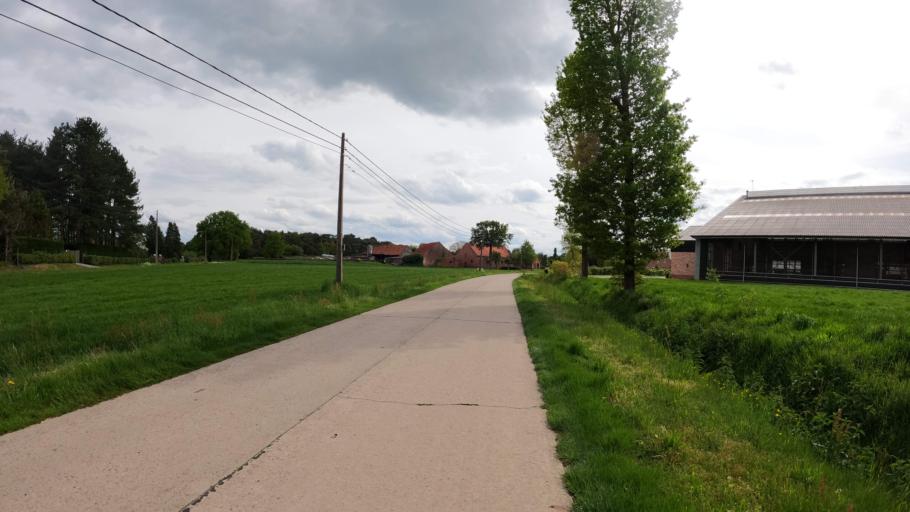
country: BE
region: Flanders
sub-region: Provincie Antwerpen
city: Vosselaar
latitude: 51.2658
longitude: 4.8983
